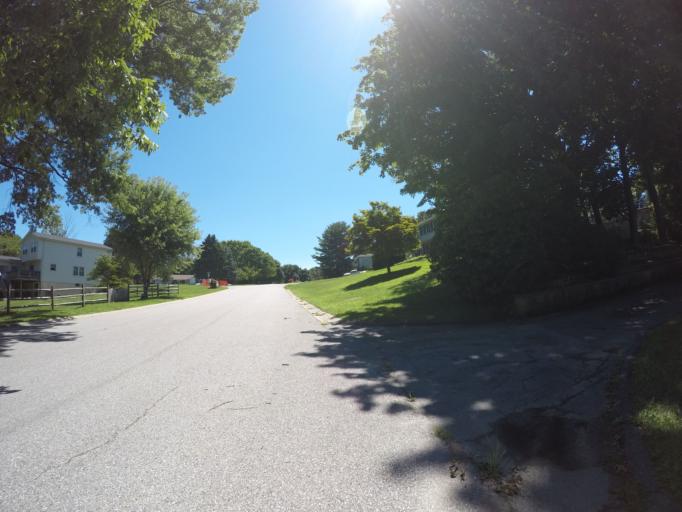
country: US
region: Maryland
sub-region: Howard County
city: Columbia
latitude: 39.2438
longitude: -76.8235
